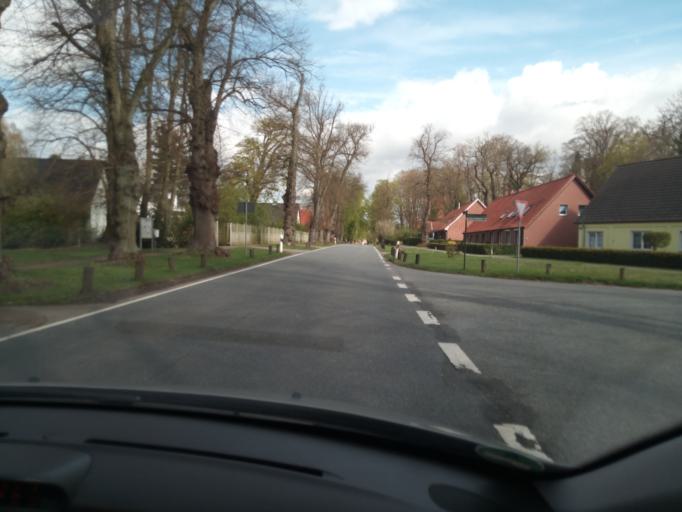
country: DE
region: Mecklenburg-Vorpommern
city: Boizenburg
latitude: 53.4259
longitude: 10.7469
